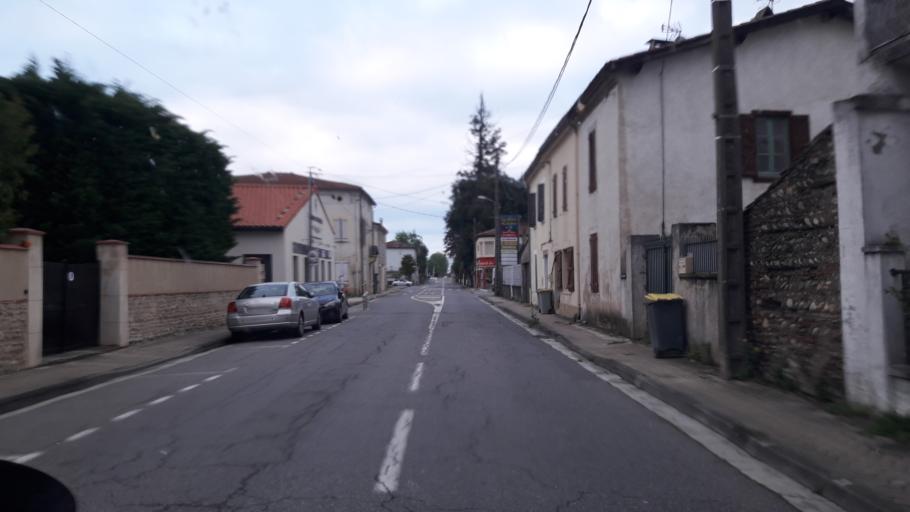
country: FR
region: Midi-Pyrenees
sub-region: Departement de la Haute-Garonne
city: Cazeres
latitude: 43.2100
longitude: 1.0856
